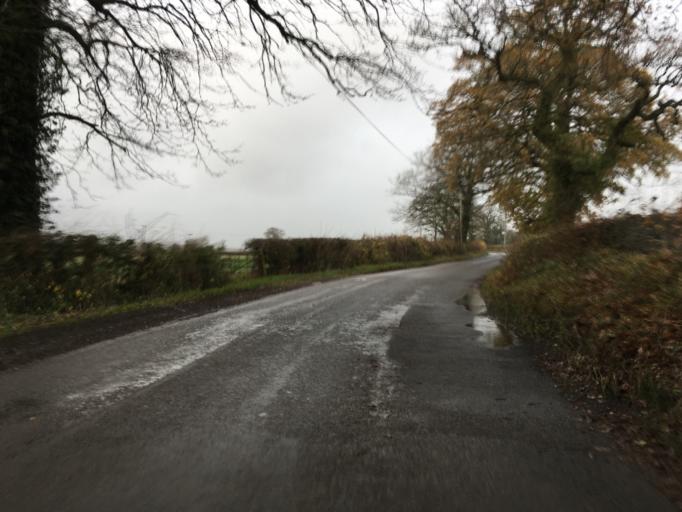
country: GB
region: England
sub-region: Wiltshire
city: Luckington
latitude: 51.5259
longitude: -2.2107
